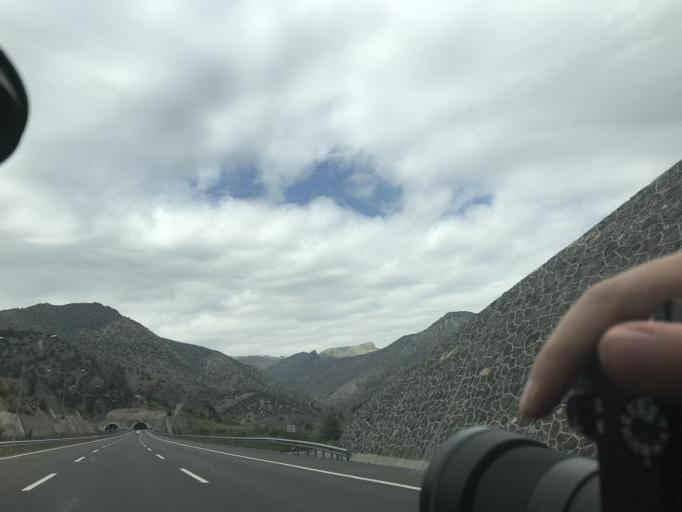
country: TR
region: Nigde
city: Ciftehan
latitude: 37.5153
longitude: 34.8177
